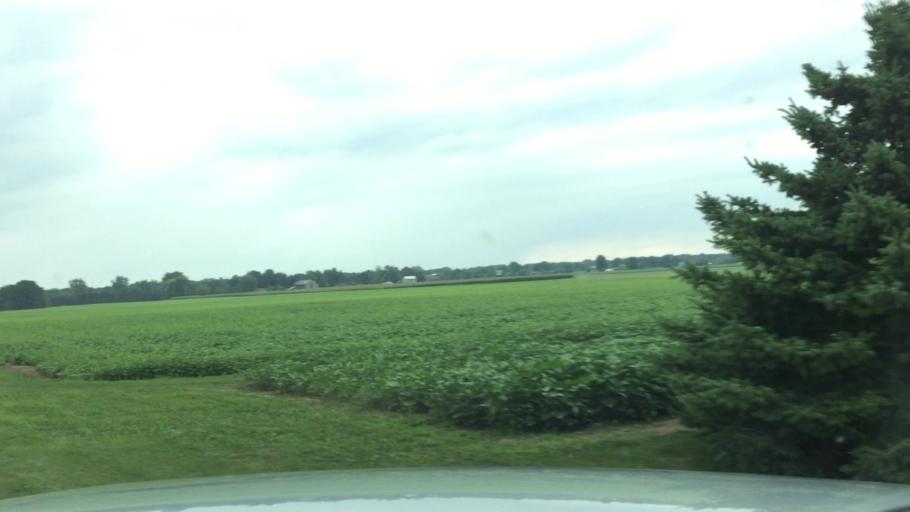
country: US
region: Michigan
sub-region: Saginaw County
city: Frankenmuth
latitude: 43.3433
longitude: -83.7787
